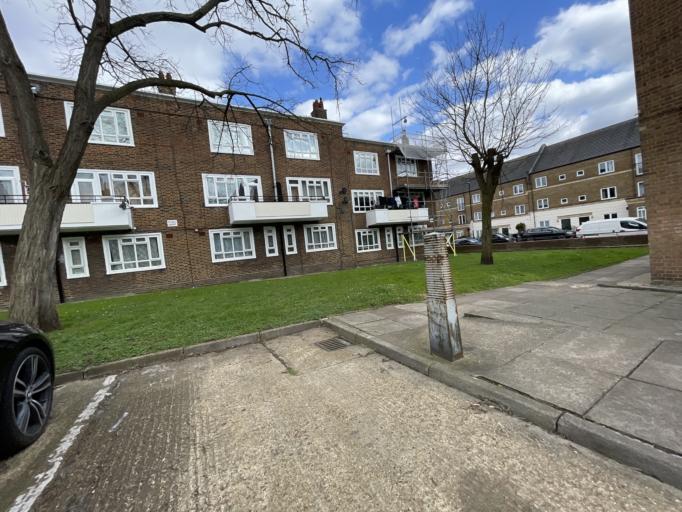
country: GB
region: England
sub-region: Greater London
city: Holloway
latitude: 51.5624
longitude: -0.1214
